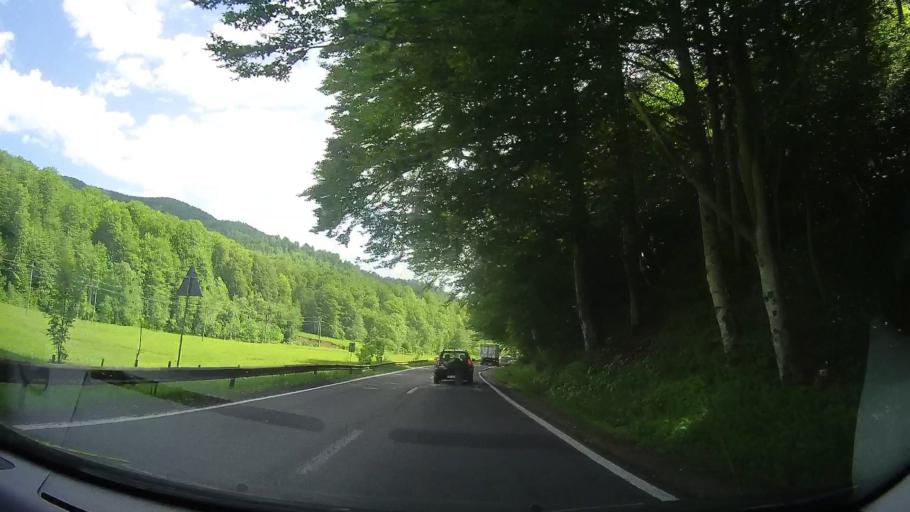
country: RO
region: Prahova
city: Maneciu
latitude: 45.3978
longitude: 25.9327
